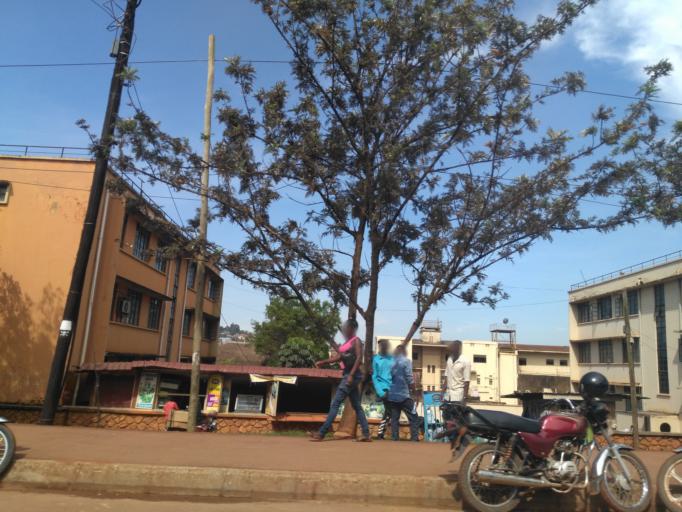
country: UG
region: Central Region
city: Kampala Central Division
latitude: 0.3211
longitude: 32.5750
